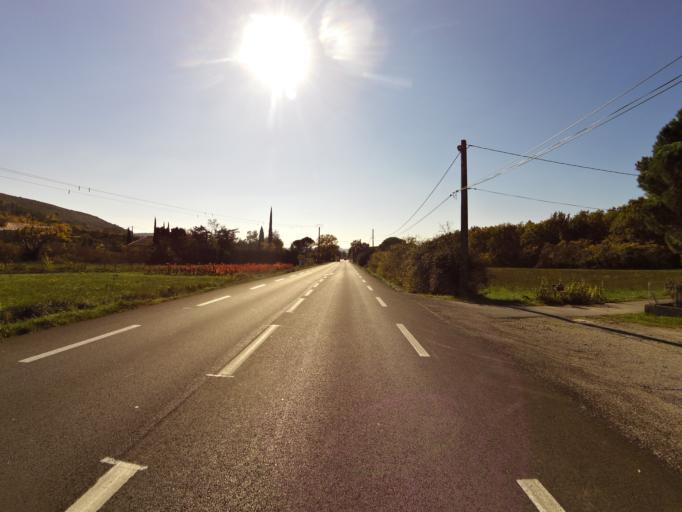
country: FR
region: Rhone-Alpes
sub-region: Departement de l'Ardeche
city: Saint-Privat
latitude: 44.6370
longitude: 4.4248
